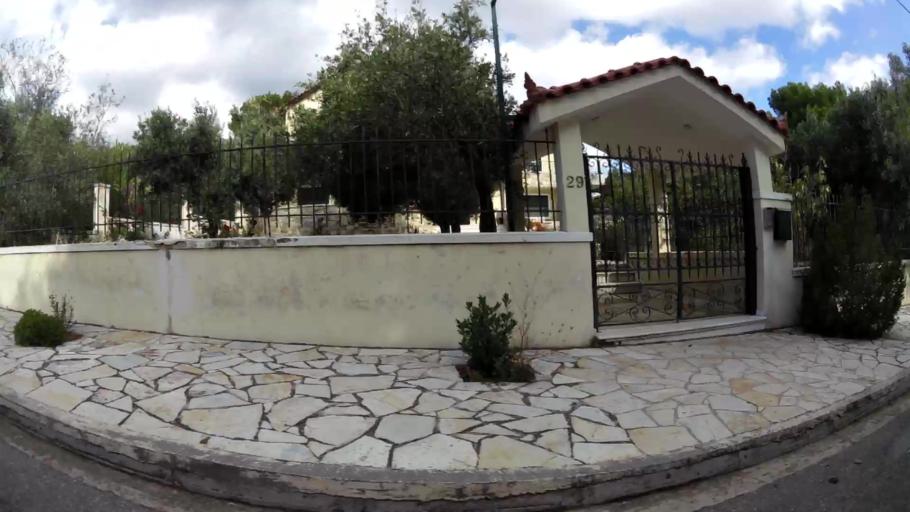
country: GR
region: Attica
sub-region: Nomarchia Anatolikis Attikis
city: Thrakomakedones
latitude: 38.1311
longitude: 23.7539
